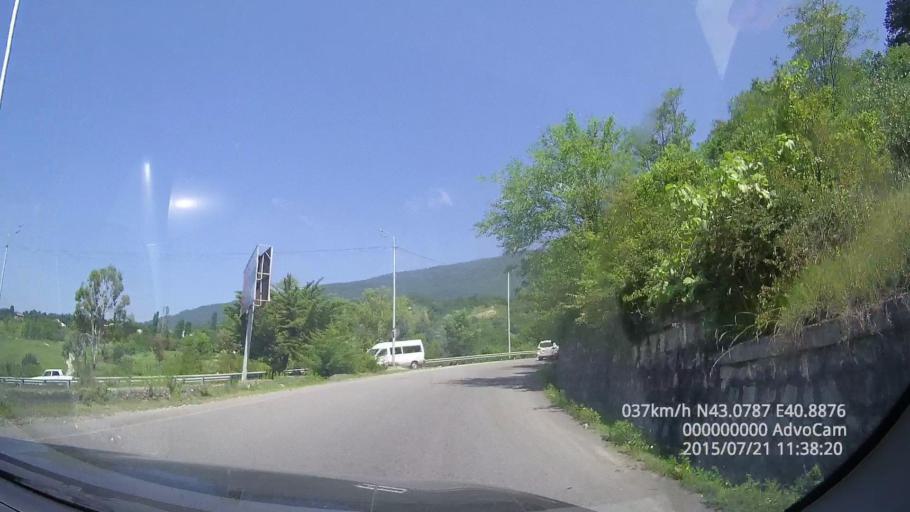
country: GE
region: Abkhazia
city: Stantsiya Novyy Afon
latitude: 43.0790
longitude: 40.8873
